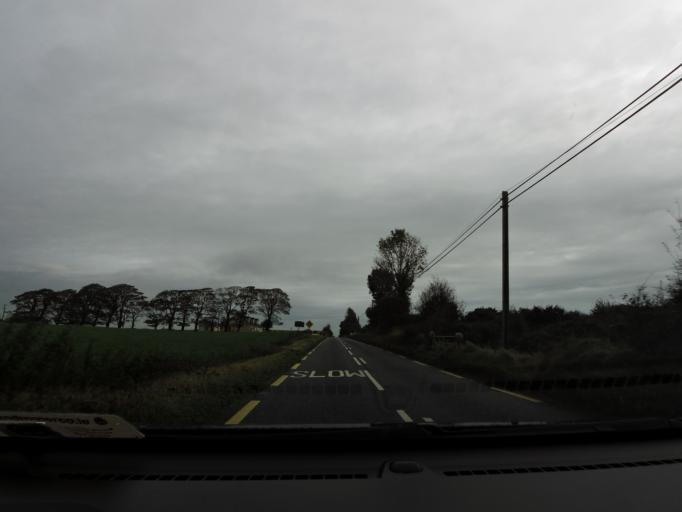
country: IE
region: Connaught
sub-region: County Galway
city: Tuam
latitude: 53.5857
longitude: -8.7786
